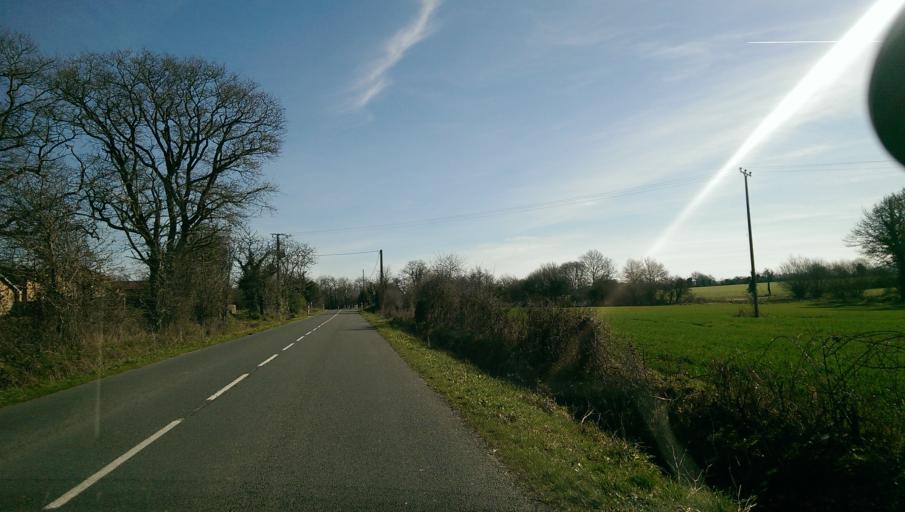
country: FR
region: Pays de la Loire
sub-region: Departement de la Vendee
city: Beaurepaire
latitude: 46.9272
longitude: -1.1130
